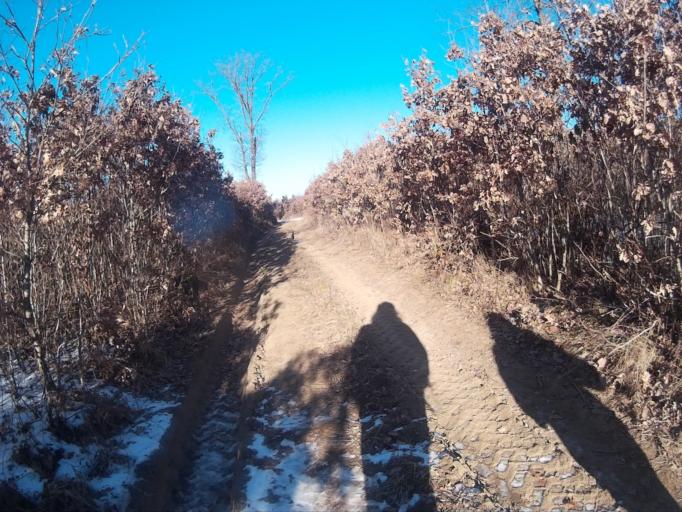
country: HU
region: Borsod-Abauj-Zemplen
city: Putnok
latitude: 48.4141
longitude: 20.4810
